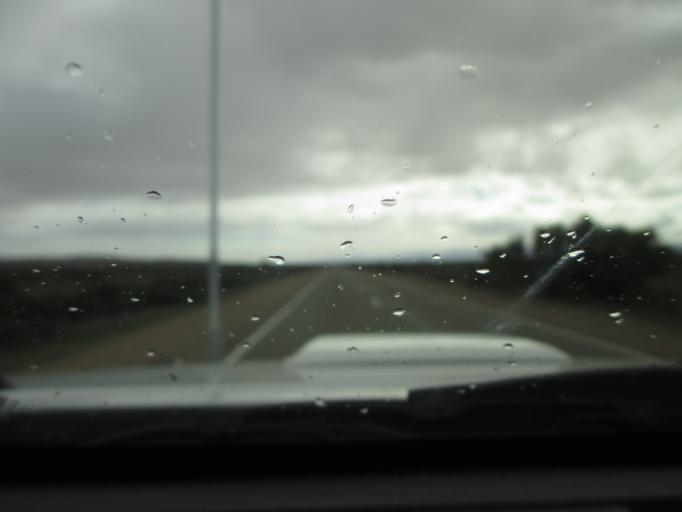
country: AU
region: South Australia
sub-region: Flinders Ranges
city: Quorn
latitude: -31.5217
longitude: 138.4270
